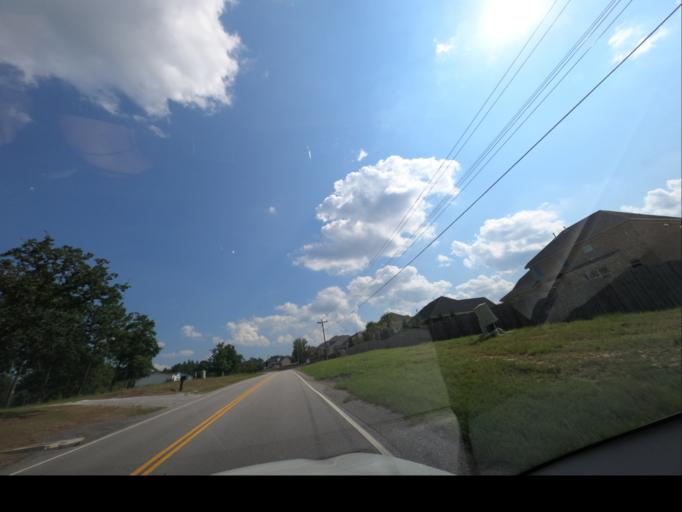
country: US
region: South Carolina
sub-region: Lexington County
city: South Congaree
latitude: 33.9026
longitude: -81.1608
